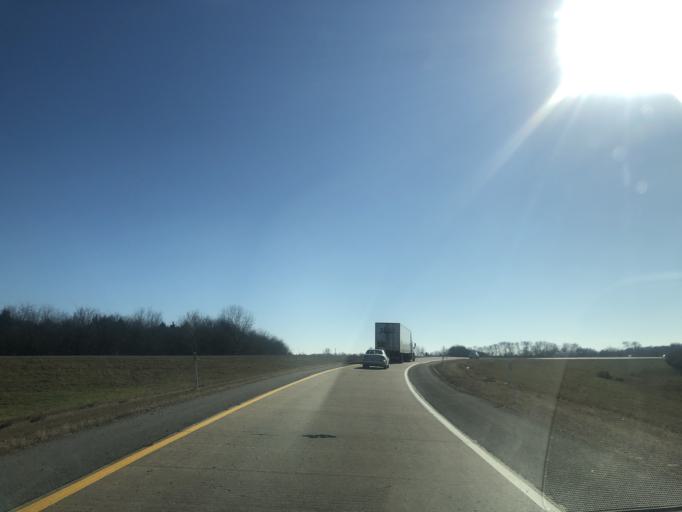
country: US
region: Tennessee
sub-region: Rutherford County
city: Murfreesboro
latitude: 35.8856
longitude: -86.4793
